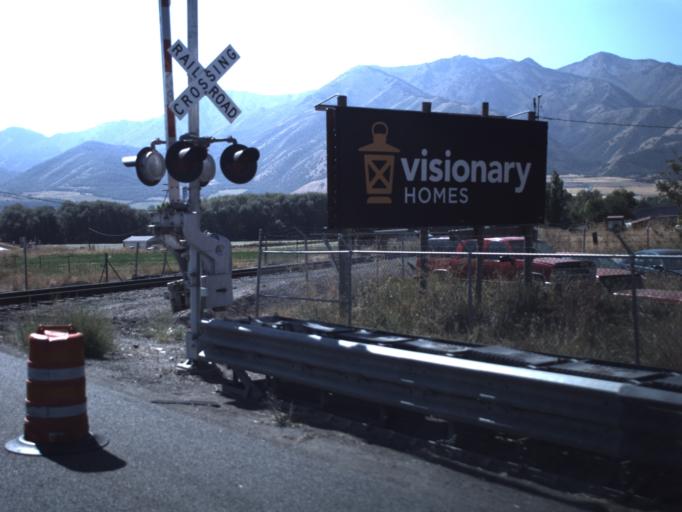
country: US
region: Utah
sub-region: Cache County
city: Wellsville
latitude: 41.6462
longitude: -111.9130
